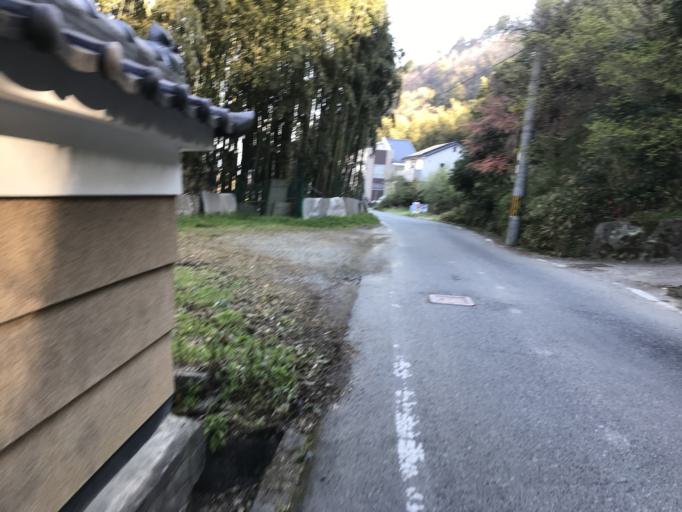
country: JP
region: Kyoto
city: Kameoka
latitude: 35.0021
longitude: 135.5573
